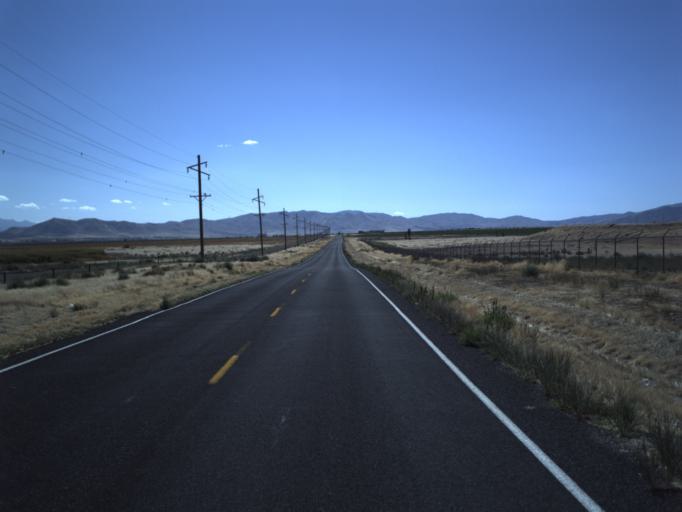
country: US
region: Utah
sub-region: Utah County
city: Genola
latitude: 40.0303
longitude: -111.9583
